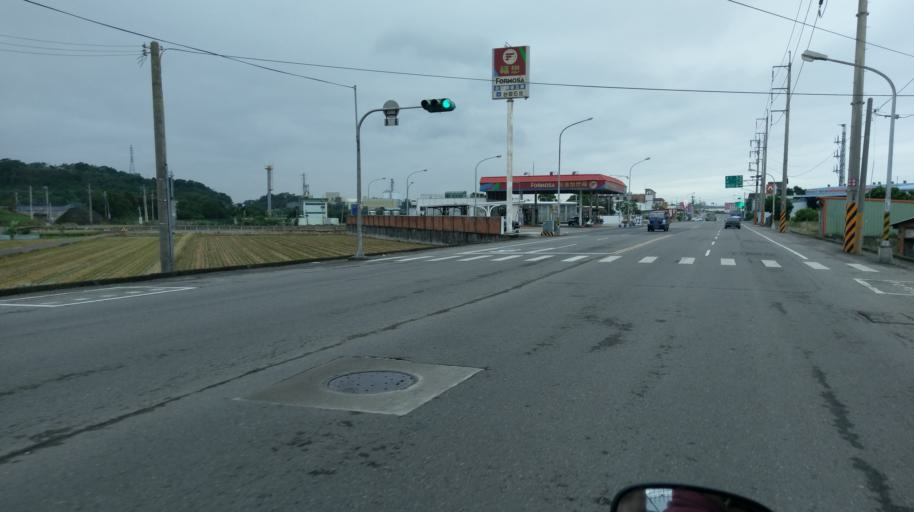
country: TW
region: Taiwan
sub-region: Miaoli
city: Miaoli
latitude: 24.6716
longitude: 120.8869
